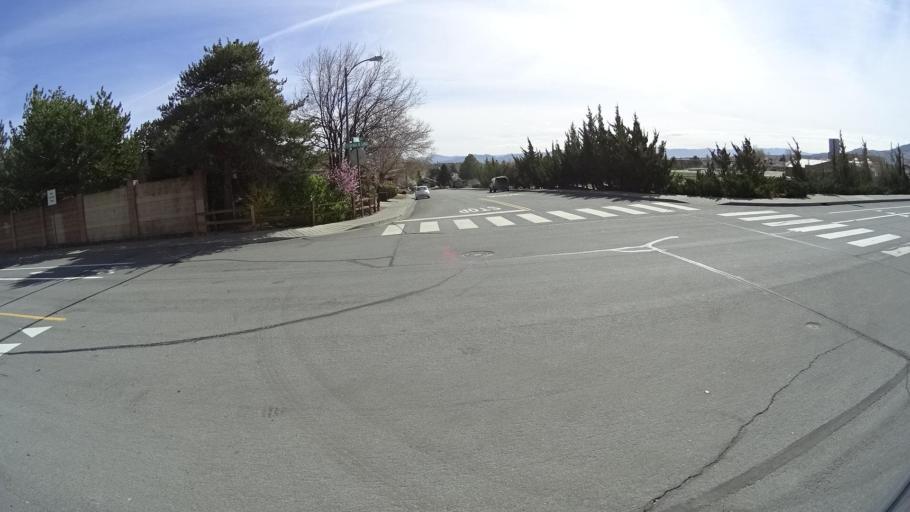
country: US
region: Nevada
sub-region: Washoe County
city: Mogul
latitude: 39.5238
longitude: -119.8953
